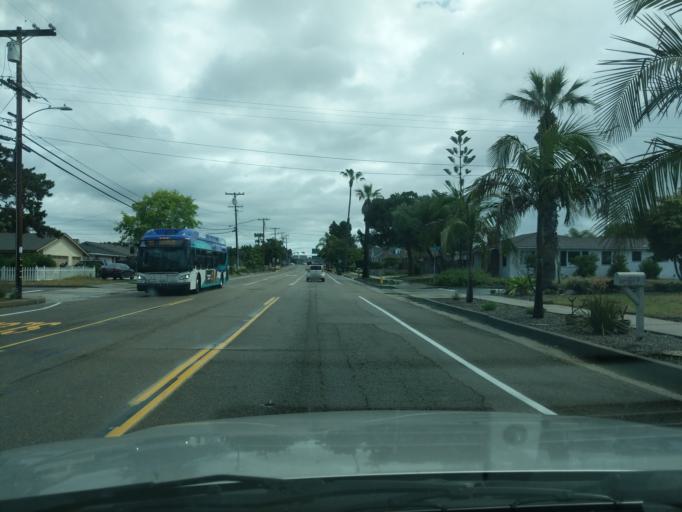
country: US
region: California
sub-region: San Diego County
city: Carlsbad
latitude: 33.1748
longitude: -117.3549
